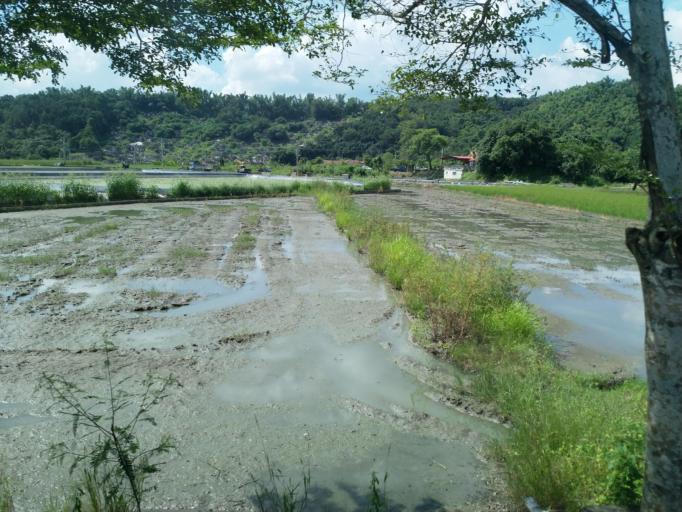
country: TW
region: Taiwan
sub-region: Pingtung
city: Pingtung
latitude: 22.8992
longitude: 120.5793
